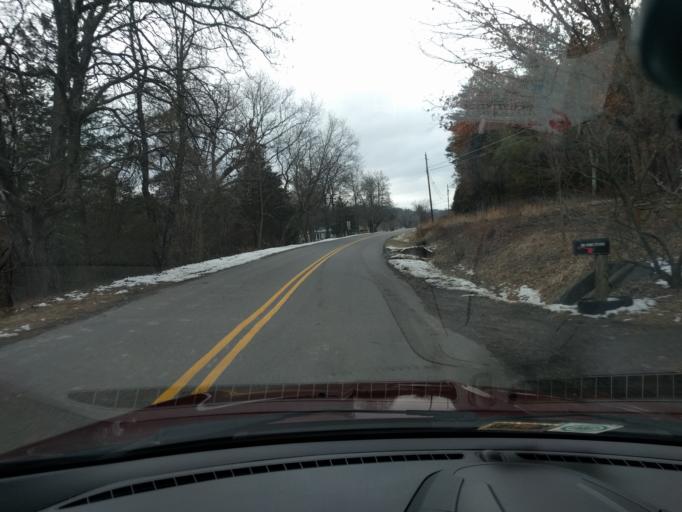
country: US
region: Virginia
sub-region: Alleghany County
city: Clifton Forge
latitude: 37.8406
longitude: -79.7478
